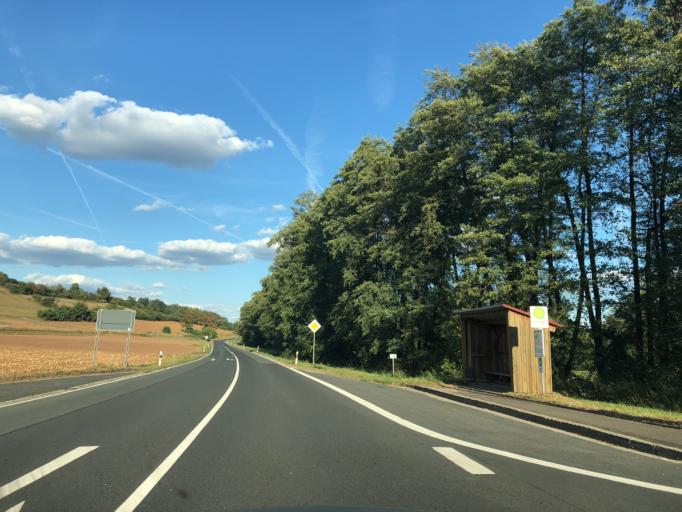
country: DE
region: Bavaria
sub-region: Upper Franconia
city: Burgwindheim
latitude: 49.8308
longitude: 10.5692
